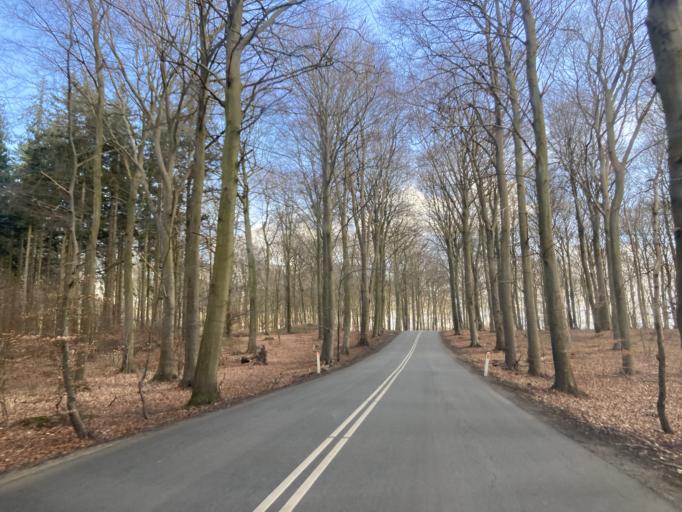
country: DK
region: Zealand
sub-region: Lejre Kommune
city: Ejby
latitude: 55.7322
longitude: 11.8853
